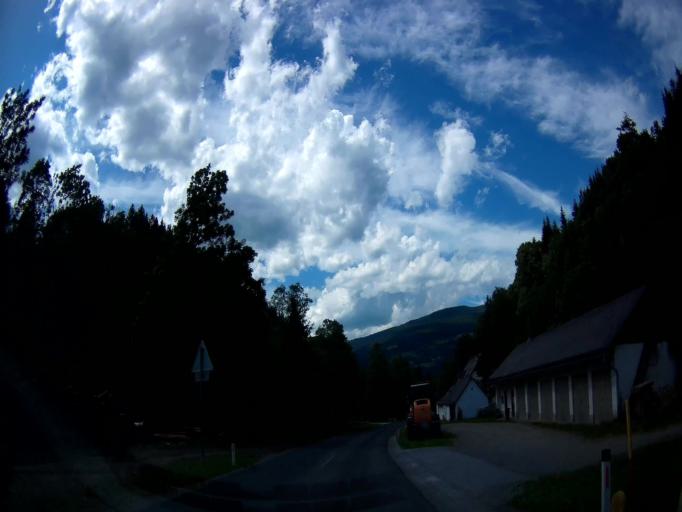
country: AT
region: Styria
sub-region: Politischer Bezirk Murau
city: Stadl an der Mur
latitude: 47.0675
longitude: 13.9858
